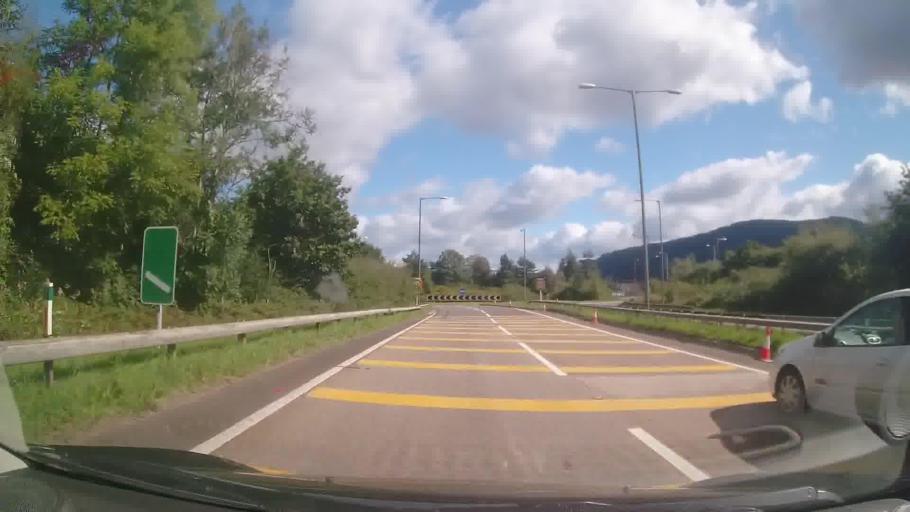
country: GB
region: Wales
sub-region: Neath Port Talbot
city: Resolven
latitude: 51.7131
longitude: -3.7002
